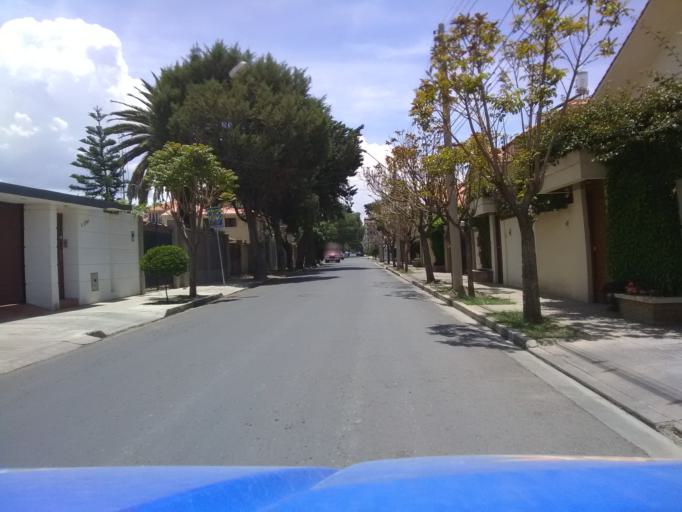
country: BO
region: Cochabamba
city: Cochabamba
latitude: -17.3785
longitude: -66.1855
